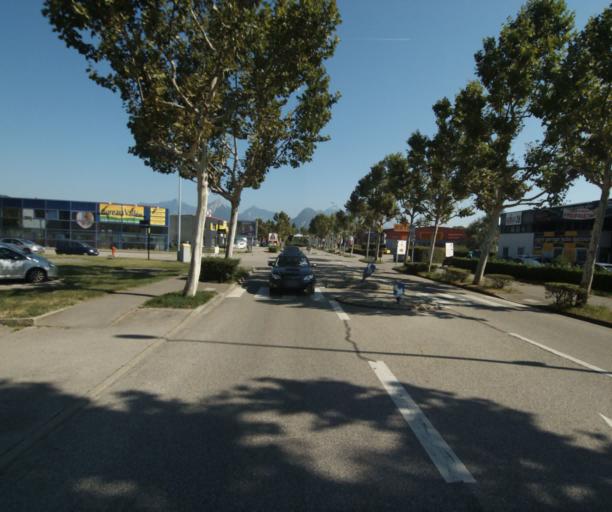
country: FR
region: Rhone-Alpes
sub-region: Departement de l'Isere
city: Seyssins
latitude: 45.1458
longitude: 5.6933
